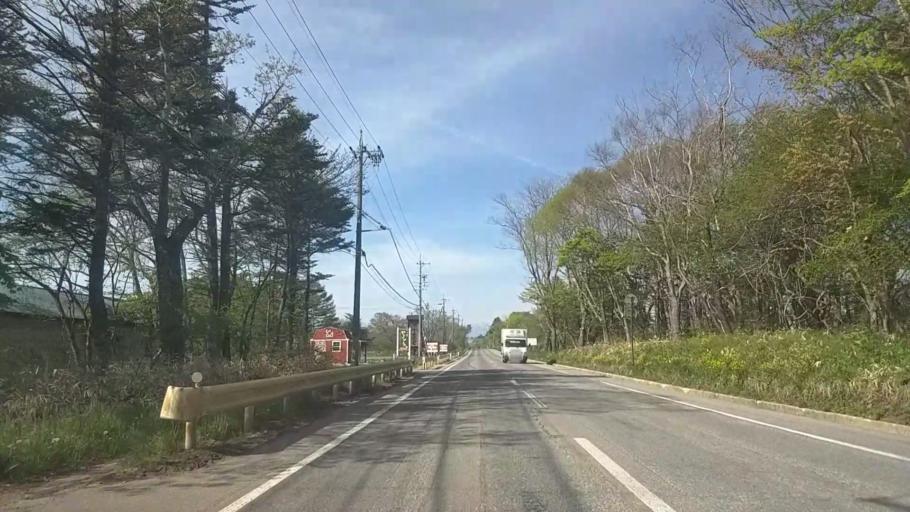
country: JP
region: Yamanashi
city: Nirasaki
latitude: 35.9534
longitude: 138.4610
